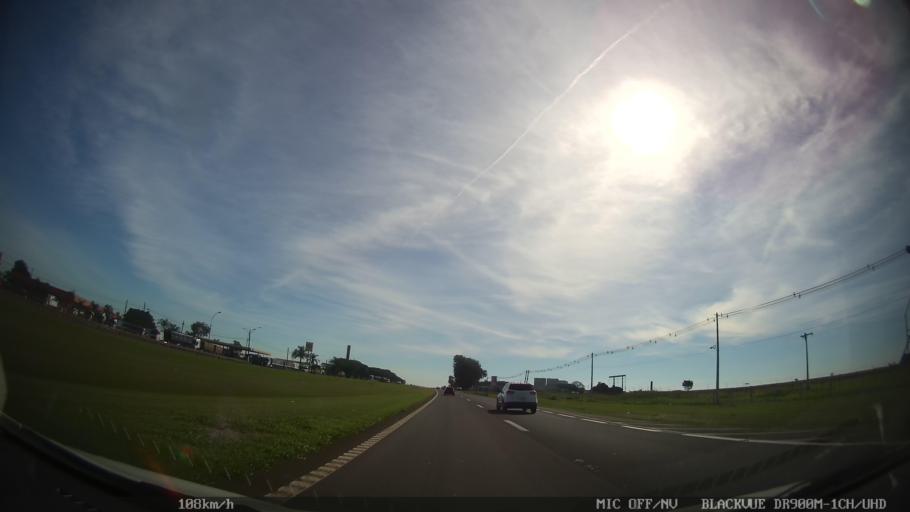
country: BR
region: Sao Paulo
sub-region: Araras
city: Araras
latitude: -22.4133
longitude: -47.3898
